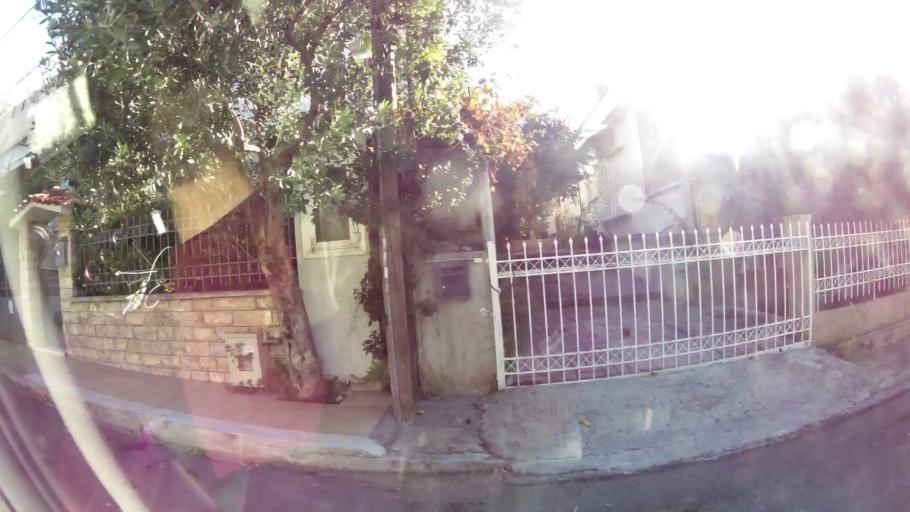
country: GR
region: Attica
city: Pefki
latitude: 38.0531
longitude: 23.7812
